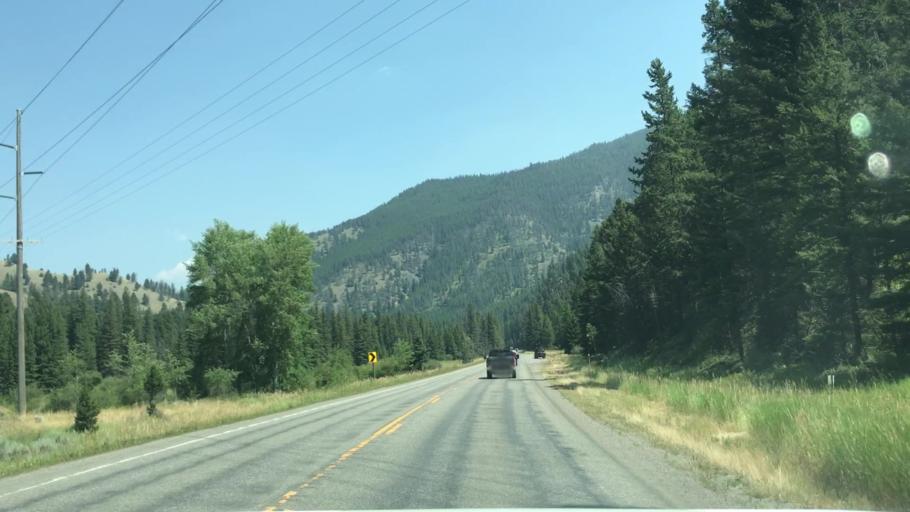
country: US
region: Montana
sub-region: Gallatin County
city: Big Sky
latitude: 45.2962
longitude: -111.2133
